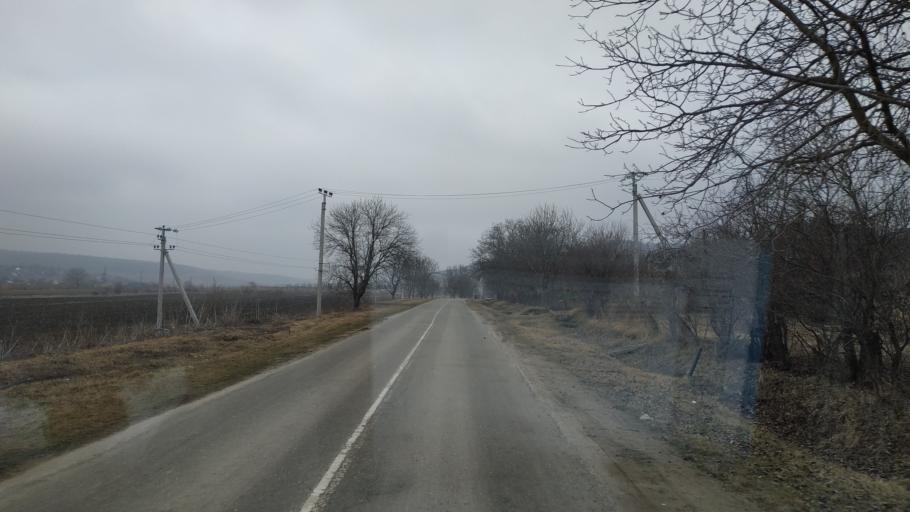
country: MD
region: Hincesti
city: Hincesti
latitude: 46.9618
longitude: 28.4848
